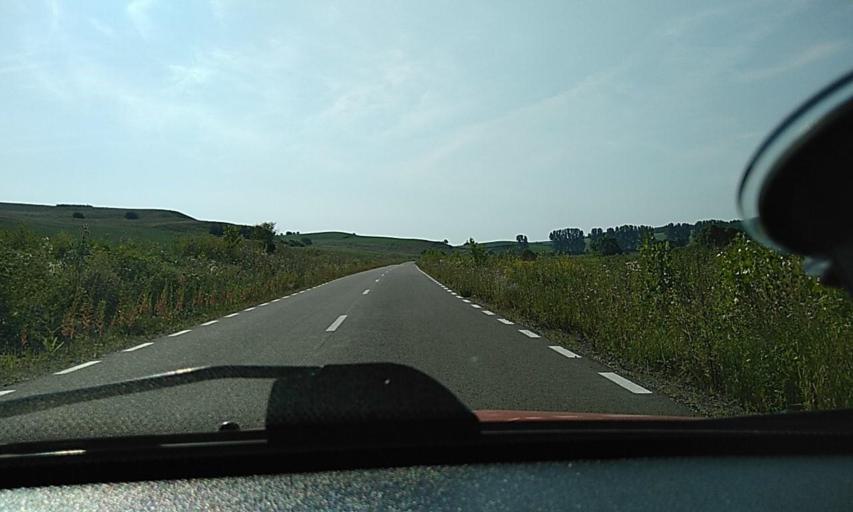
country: RO
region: Brasov
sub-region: Comuna Bunesti
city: Bunesti
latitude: 46.0726
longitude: 25.0718
